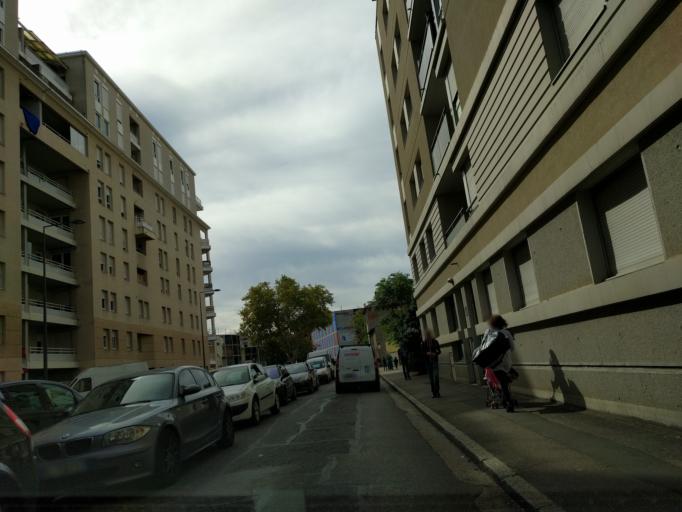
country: FR
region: Rhone-Alpes
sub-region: Departement du Rhone
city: Villeurbanne
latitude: 45.7594
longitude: 4.9002
